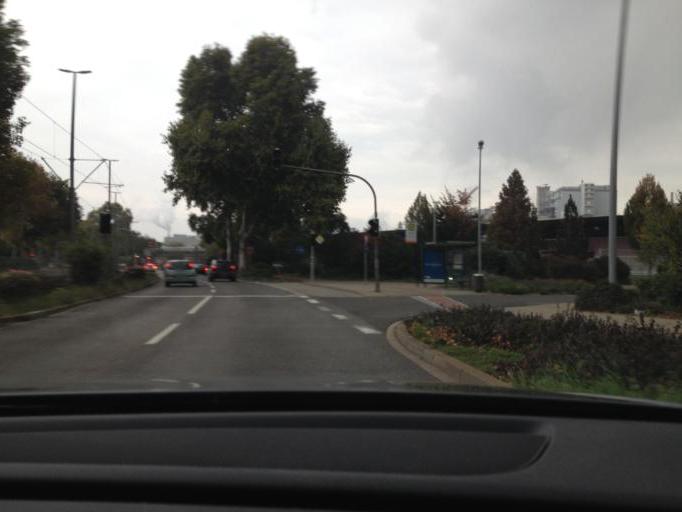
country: DE
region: Rheinland-Pfalz
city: Ludwigshafen am Rhein
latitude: 49.4996
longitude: 8.4249
